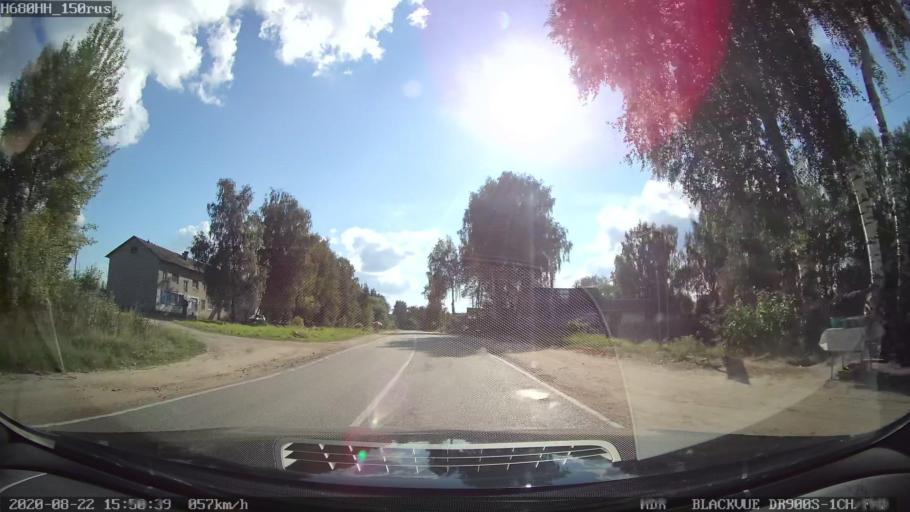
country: RU
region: Tverskaya
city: Bezhetsk
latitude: 57.6697
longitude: 36.4393
